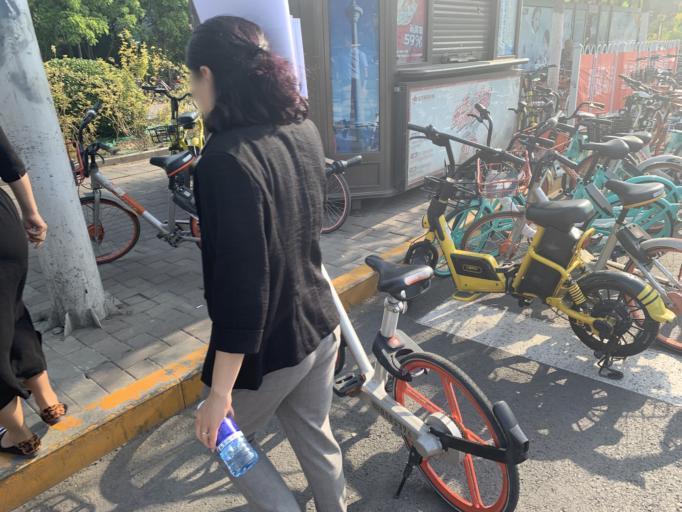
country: CN
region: Tianjin Shi
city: Xiangyanglu
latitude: 39.1365
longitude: 117.1283
